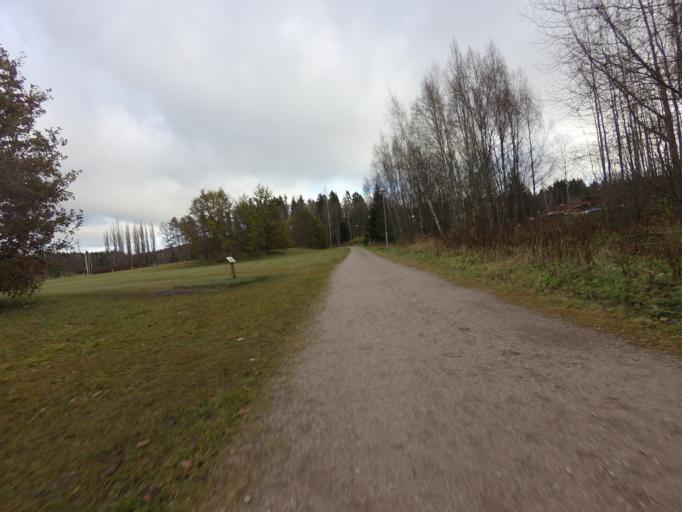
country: FI
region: Uusimaa
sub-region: Helsinki
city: Kauniainen
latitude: 60.1774
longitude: 24.7023
